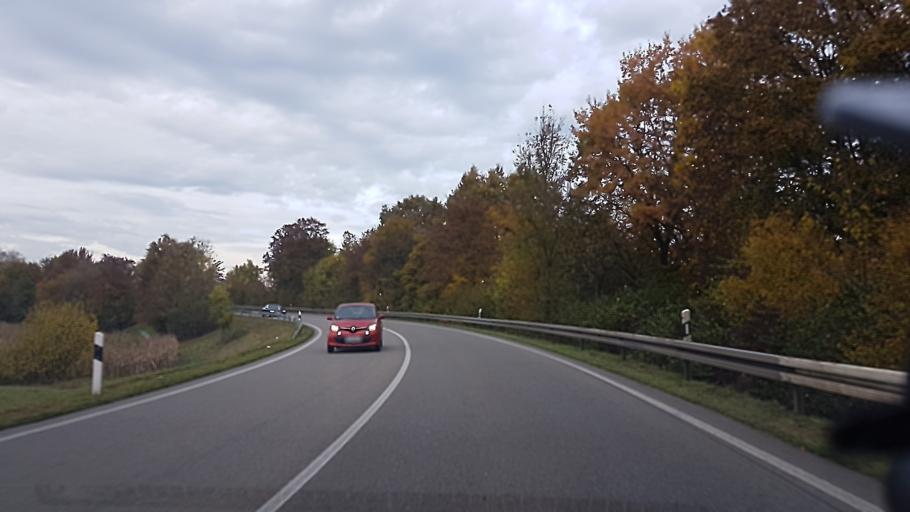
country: DE
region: Baden-Wuerttemberg
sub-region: Freiburg Region
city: Gundelfingen
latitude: 48.0466
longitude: 7.8591
